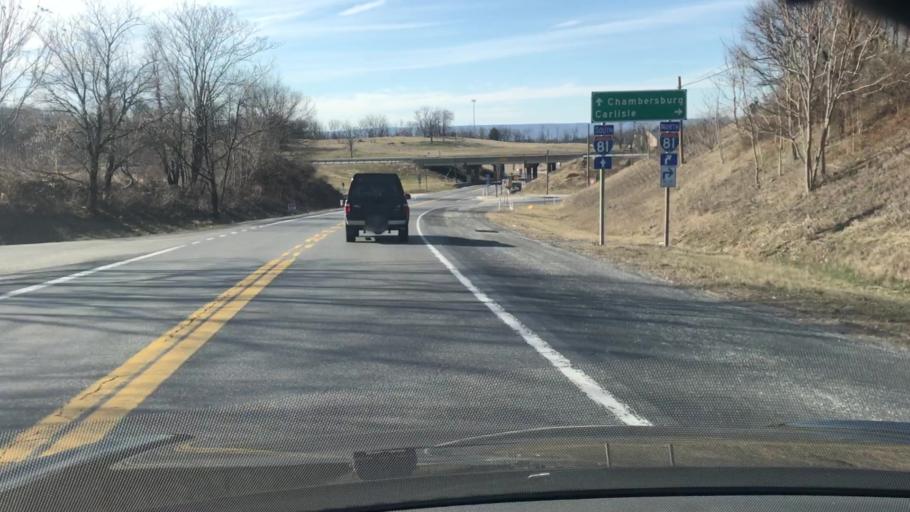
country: US
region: Pennsylvania
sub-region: Cumberland County
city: Newville
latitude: 40.1276
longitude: -77.3483
